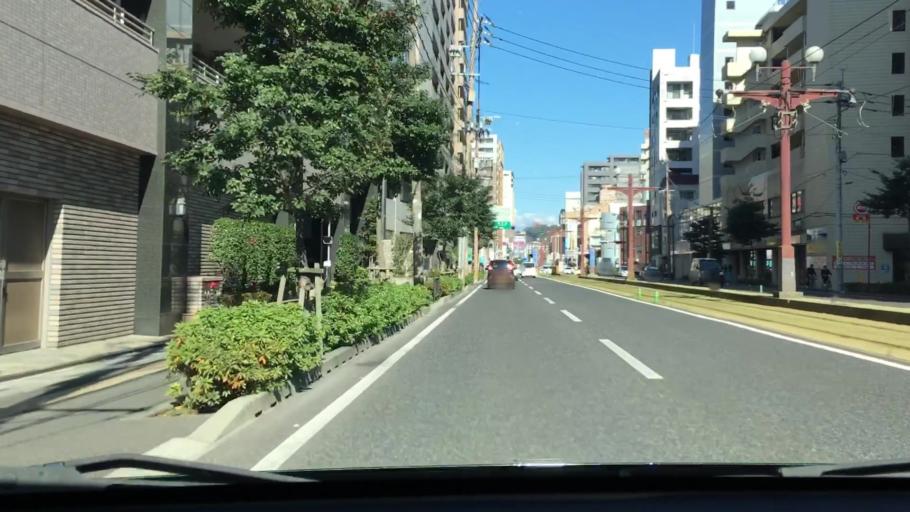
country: JP
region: Kagoshima
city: Kagoshima-shi
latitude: 31.5772
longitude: 130.5424
